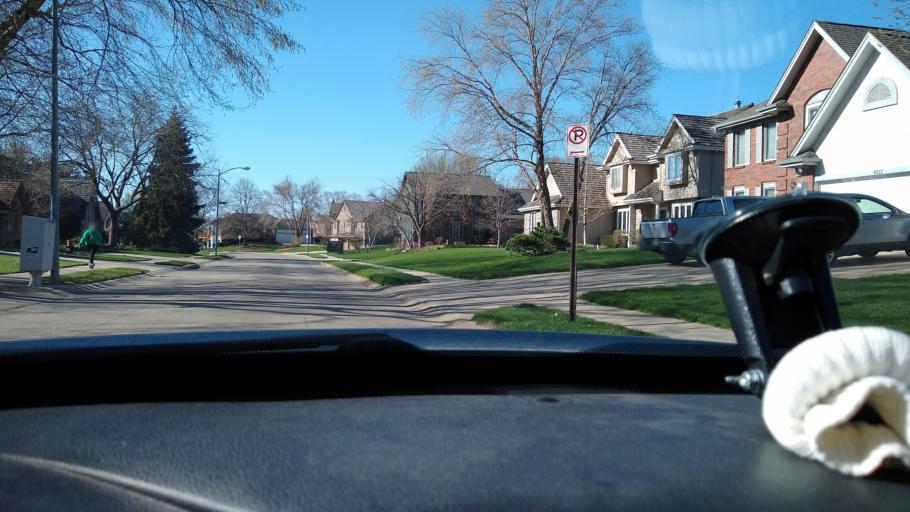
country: US
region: Nebraska
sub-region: Douglas County
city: Ralston
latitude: 41.1928
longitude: -96.0723
